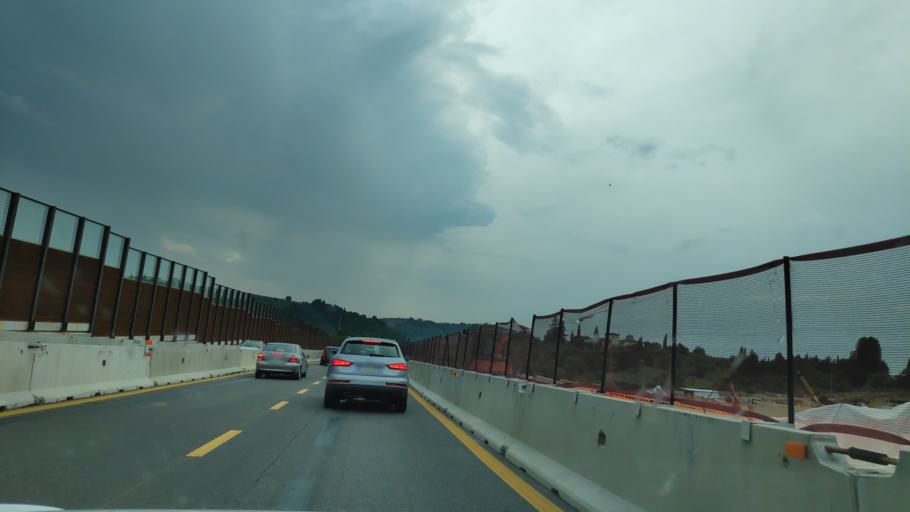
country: IT
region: Tuscany
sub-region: Province of Florence
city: Antella
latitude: 43.7295
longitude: 11.3294
